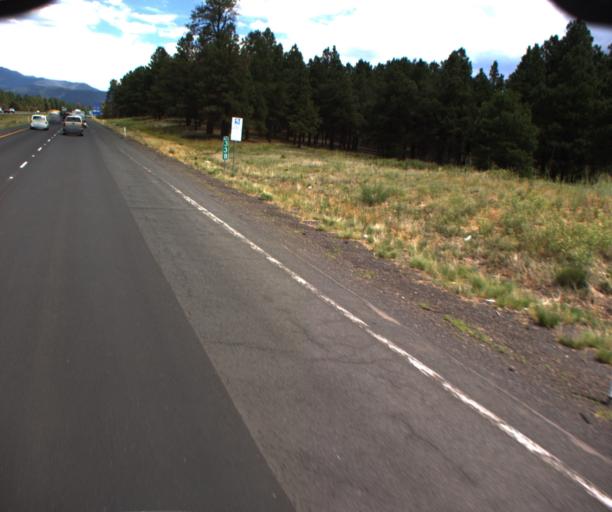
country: US
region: Arizona
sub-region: Coconino County
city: Kachina Village
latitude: 35.1480
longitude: -111.6822
